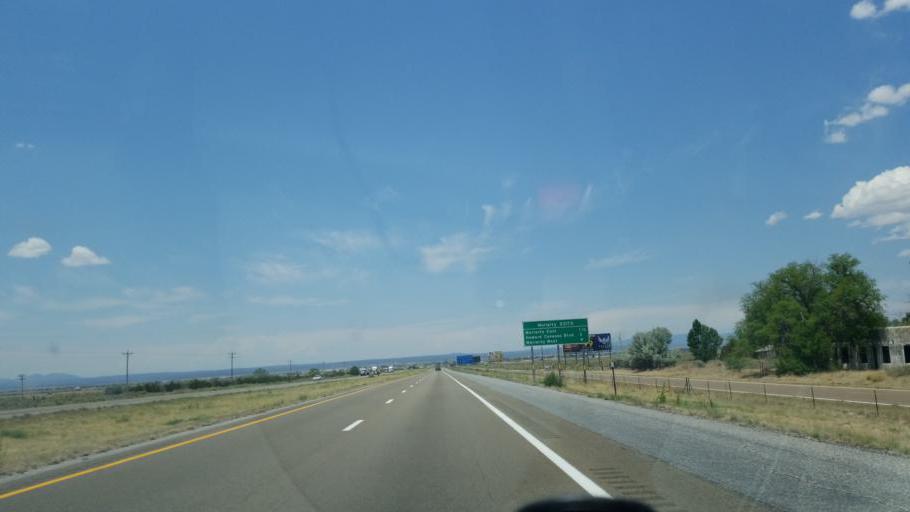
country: US
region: New Mexico
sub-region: Torrance County
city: Moriarty
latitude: 35.0049
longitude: -105.9769
